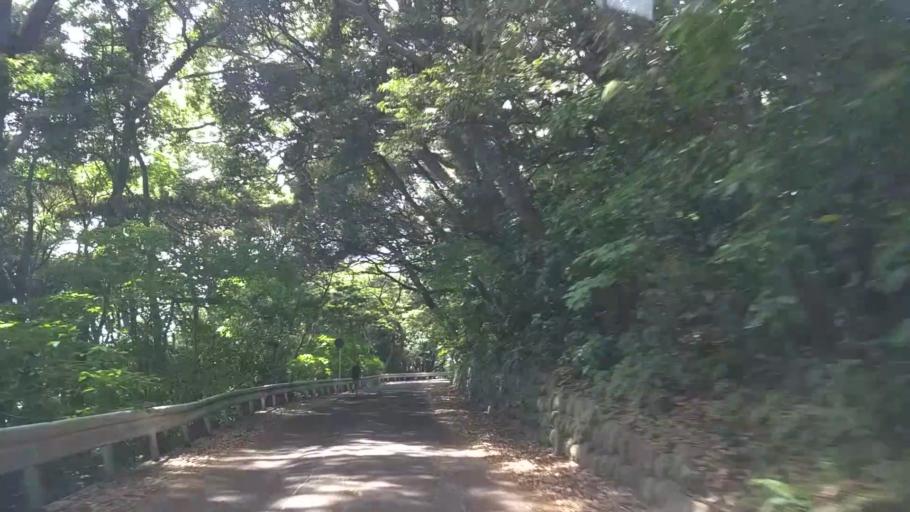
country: JP
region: Kanagawa
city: Yugawara
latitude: 35.1424
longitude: 139.1547
